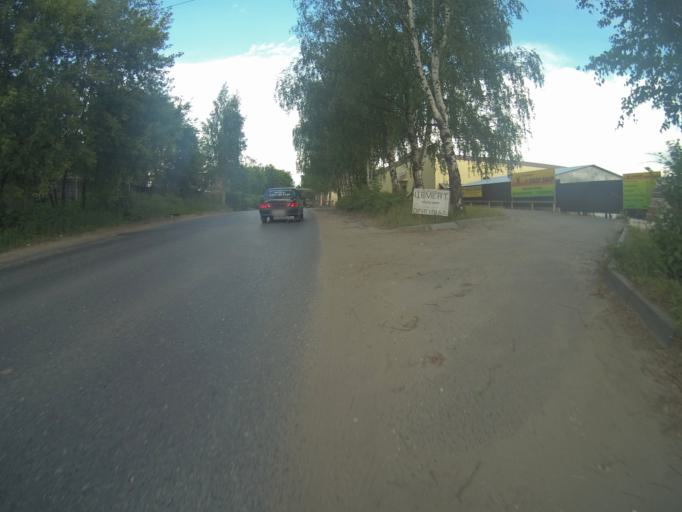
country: RU
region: Vladimir
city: Vladimir
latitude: 56.1612
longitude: 40.3802
